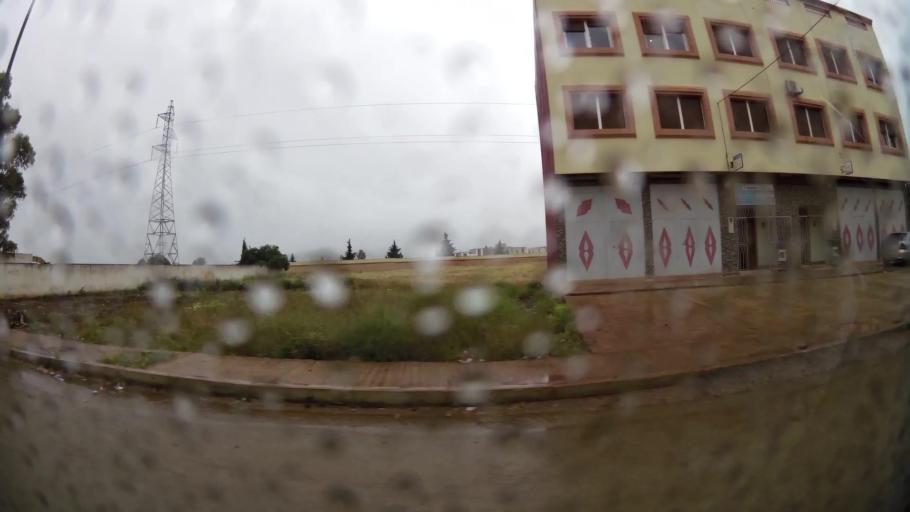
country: MA
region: Oriental
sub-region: Nador
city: Boudinar
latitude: 35.1137
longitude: -3.6435
